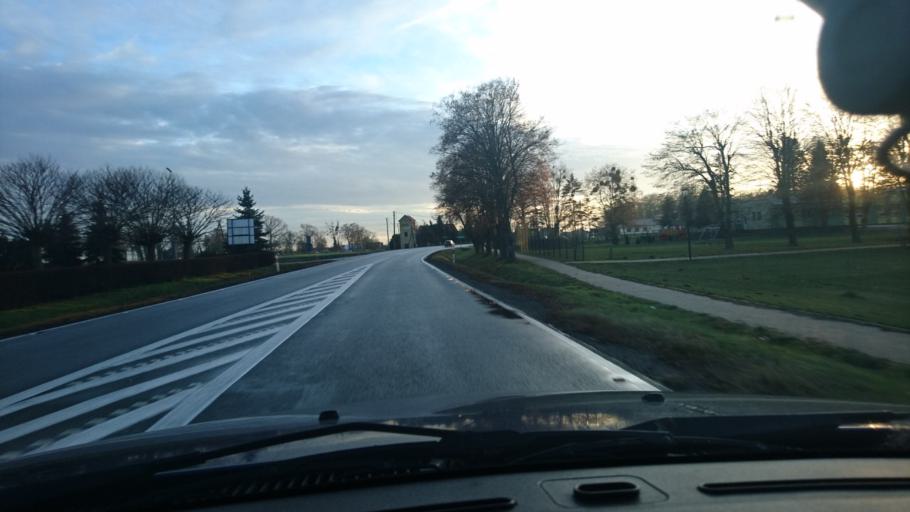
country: PL
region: Greater Poland Voivodeship
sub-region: Powiat kepinski
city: Opatow
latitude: 51.1841
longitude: 18.1464
